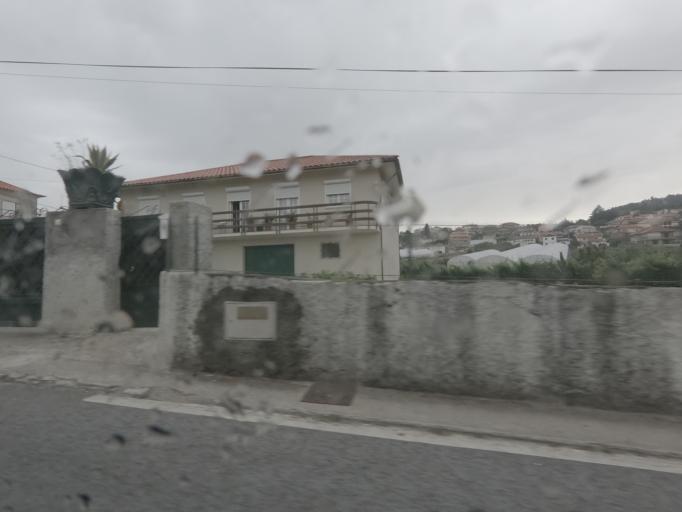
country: PT
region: Viseu
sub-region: Armamar
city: Armamar
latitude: 41.1210
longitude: -7.7305
